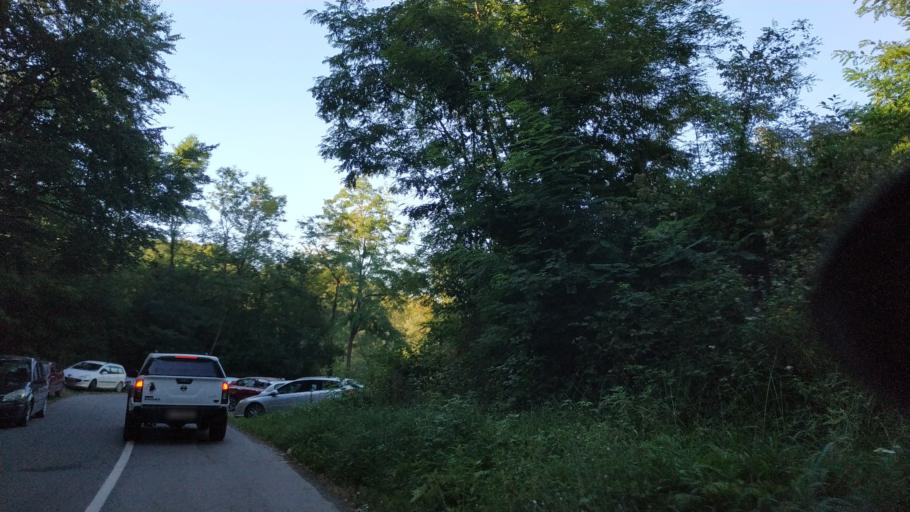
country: RS
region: Central Serbia
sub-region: Rasinski Okrug
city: Krusevac
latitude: 43.4581
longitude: 21.3590
